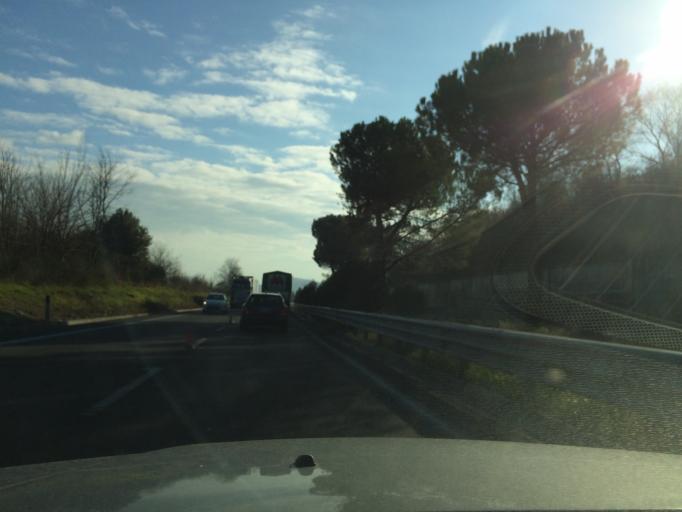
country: IT
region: Umbria
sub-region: Provincia di Terni
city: San Gemini
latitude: 42.6202
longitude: 12.5530
